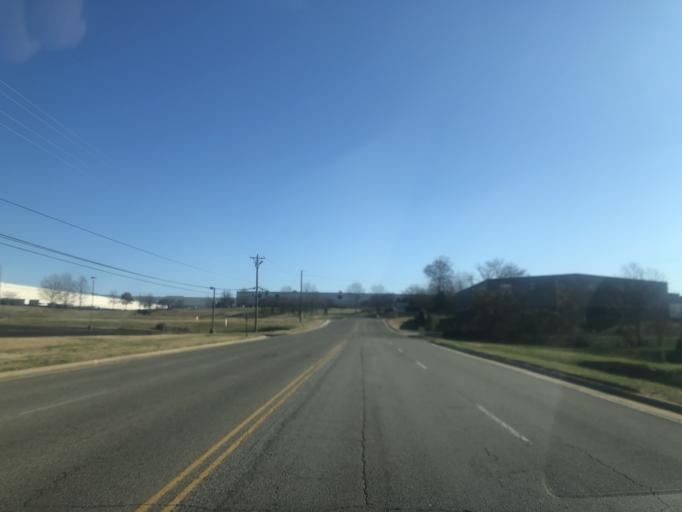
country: US
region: Tennessee
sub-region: Rutherford County
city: La Vergne
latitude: 35.9988
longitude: -86.5877
